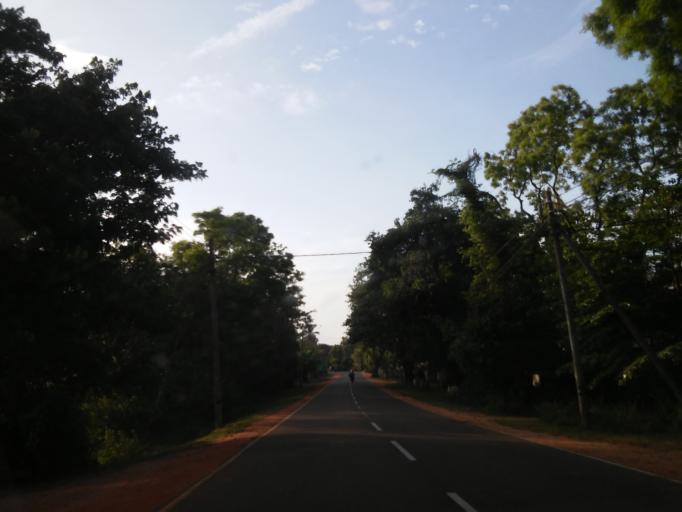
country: LK
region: Central
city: Sigiriya
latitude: 8.0945
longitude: 80.6244
